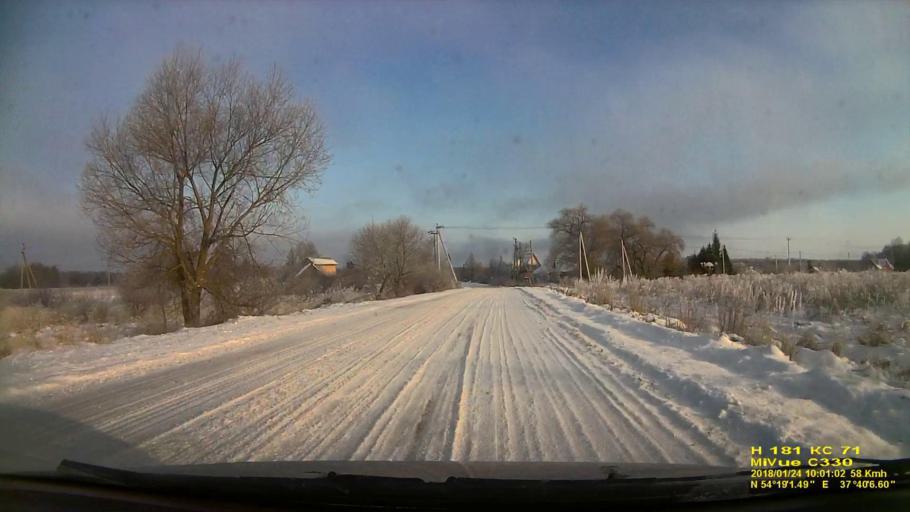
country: RU
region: Tula
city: Revyakino
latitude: 54.3172
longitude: 37.6685
